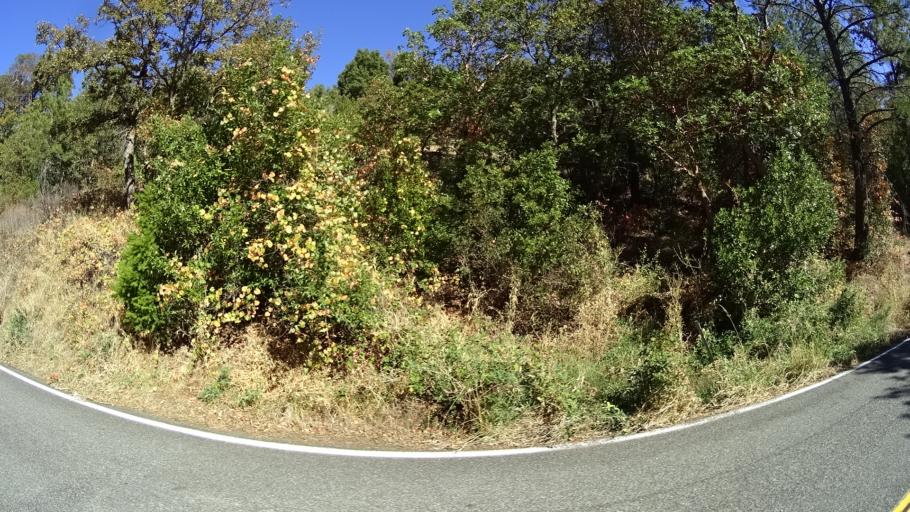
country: US
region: California
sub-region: Siskiyou County
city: Happy Camp
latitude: 41.3786
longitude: -123.4806
